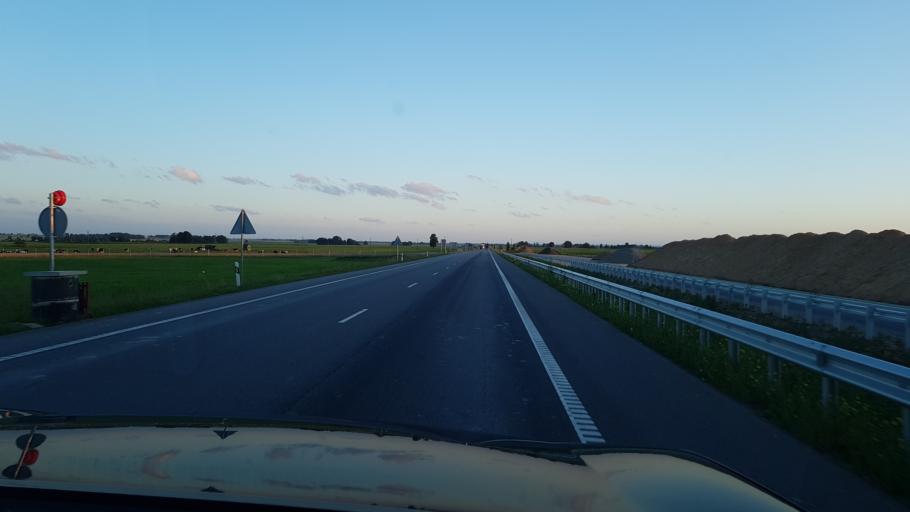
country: LT
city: Kazlu Ruda
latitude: 54.6652
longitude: 23.5136
